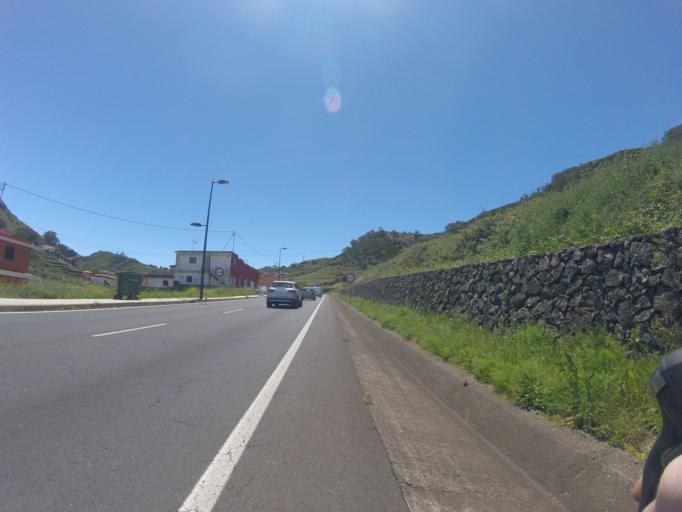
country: ES
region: Canary Islands
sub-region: Provincia de Santa Cruz de Tenerife
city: Tegueste
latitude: 28.5143
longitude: -16.3146
